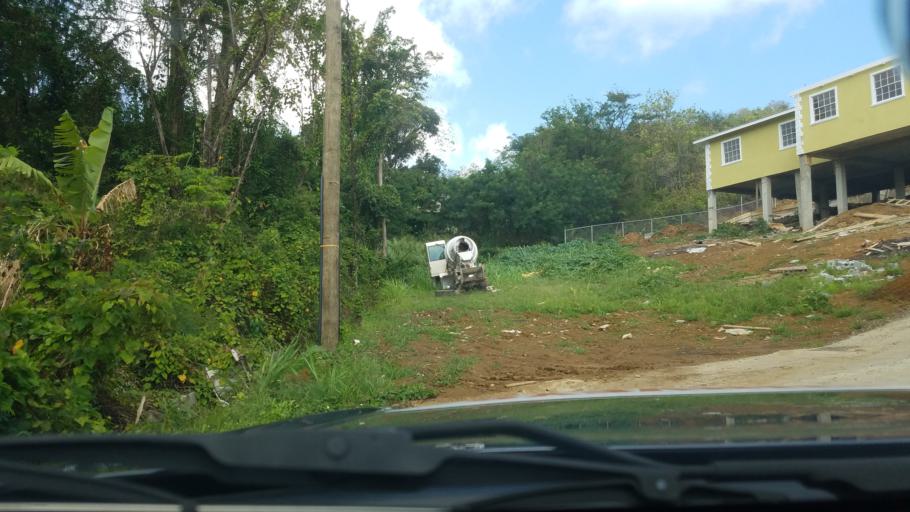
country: LC
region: Gros-Islet
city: Gros Islet
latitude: 14.0614
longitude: -60.9466
